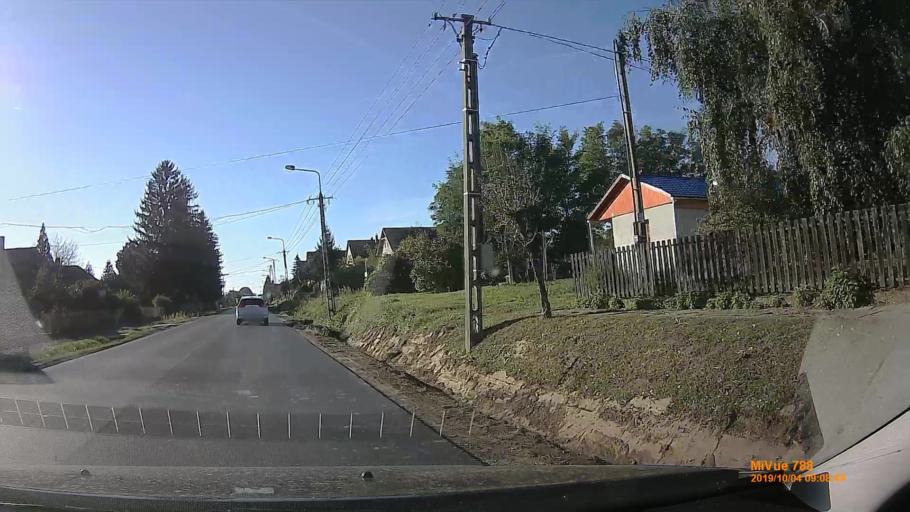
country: HU
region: Somogy
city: Karad
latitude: 46.6681
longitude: 17.7785
